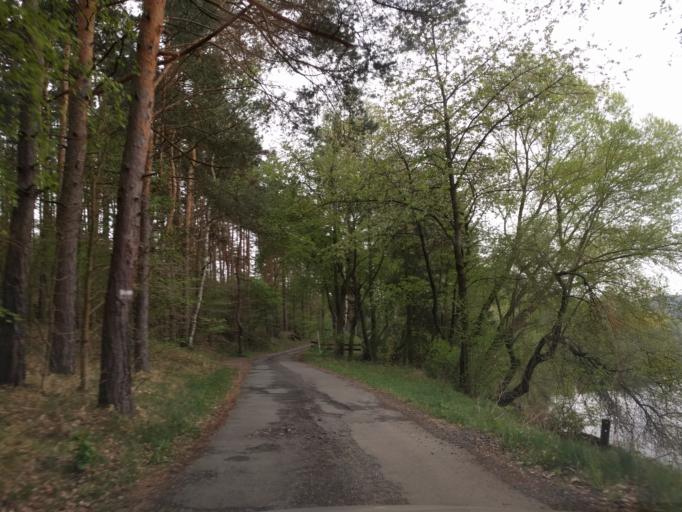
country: CZ
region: Central Bohemia
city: Krasna Hora nad Vltavou
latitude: 49.6699
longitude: 14.2624
